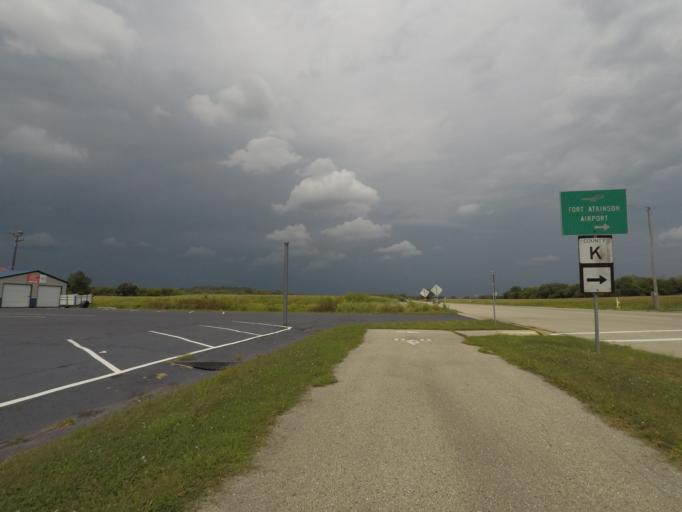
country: US
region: Wisconsin
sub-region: Jefferson County
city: Fort Atkinson
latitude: 42.9444
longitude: -88.8278
